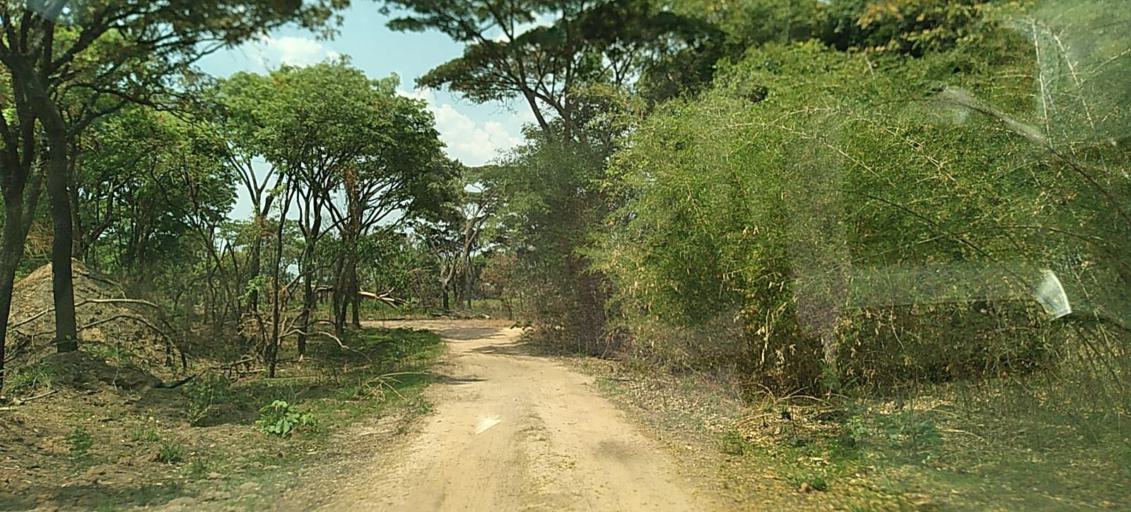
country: ZM
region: Copperbelt
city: Chingola
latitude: -12.7421
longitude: 27.7268
